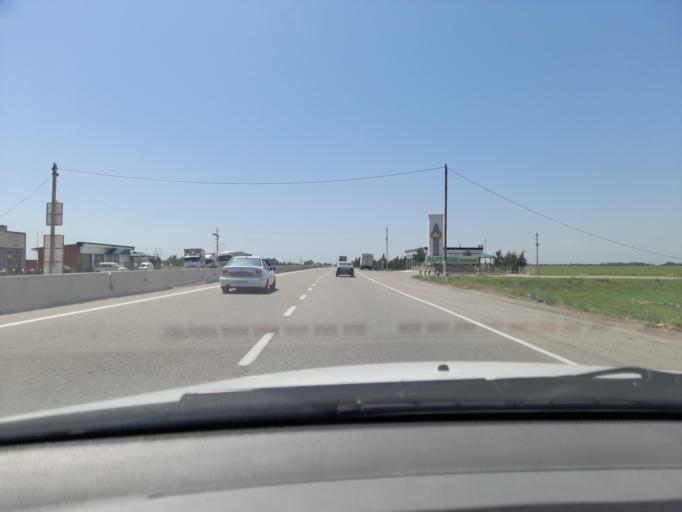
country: UZ
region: Jizzax
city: Dustlik
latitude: 40.3740
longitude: 68.1583
